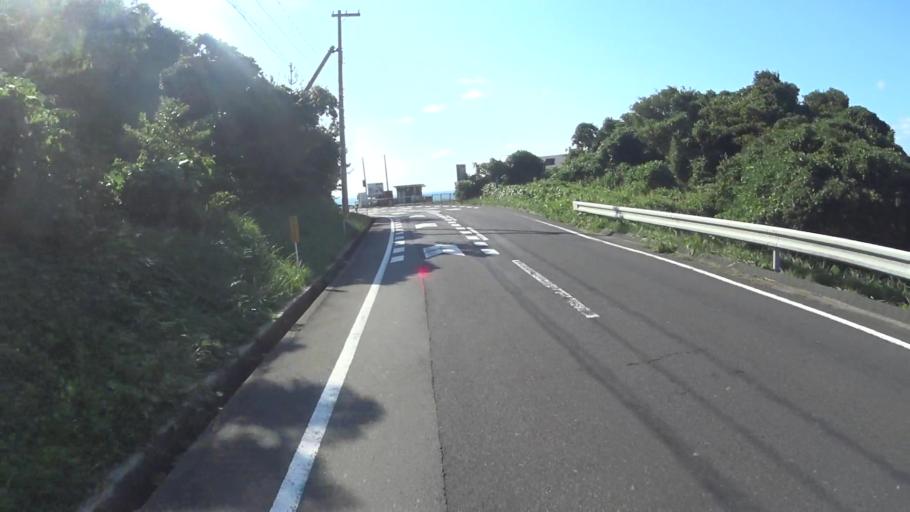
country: JP
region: Kyoto
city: Miyazu
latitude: 35.7173
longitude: 135.0701
